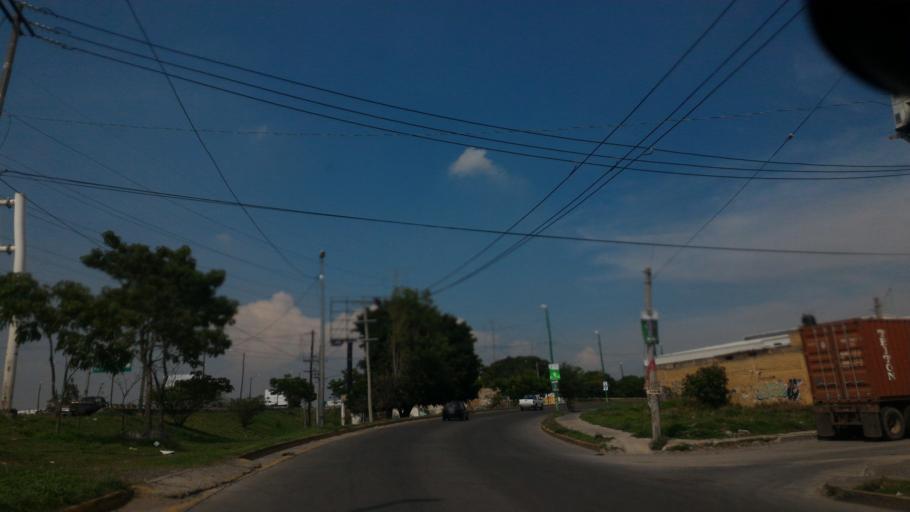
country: MX
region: Jalisco
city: Tlaquepaque
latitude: 20.6280
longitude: -103.2974
